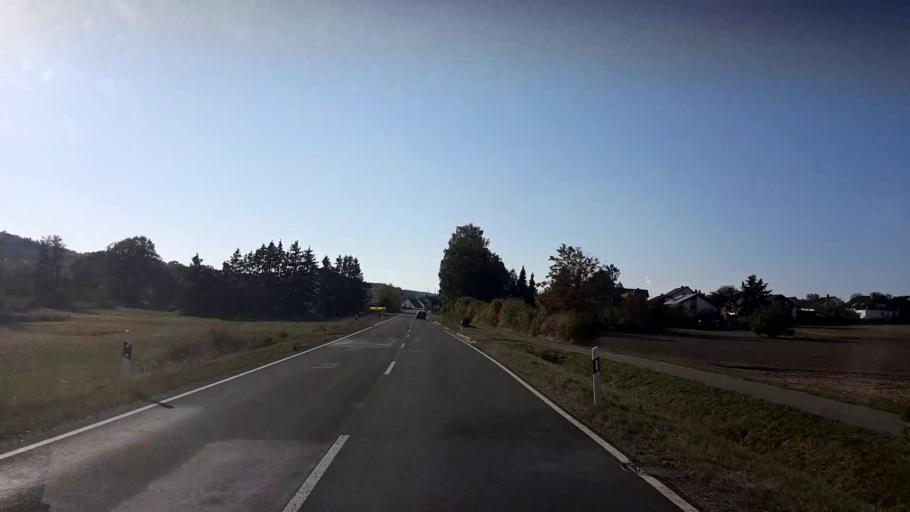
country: DE
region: Bavaria
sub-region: Upper Franconia
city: Stegaurach
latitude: 49.8702
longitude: 10.8225
